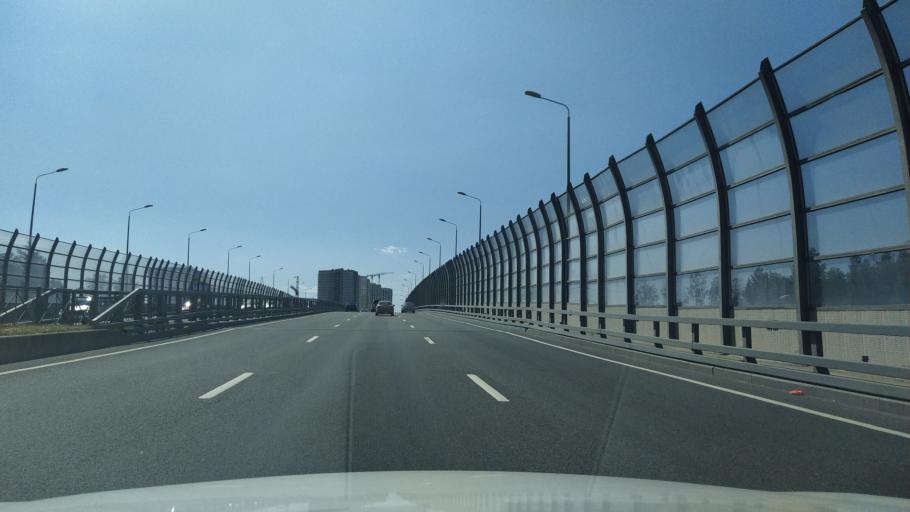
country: RU
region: St.-Petersburg
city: Shuvalovo
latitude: 60.0624
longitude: 30.2850
